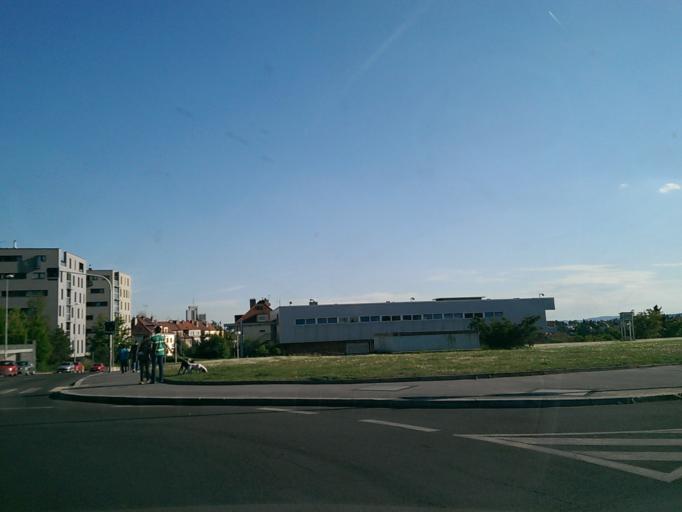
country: CZ
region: Praha
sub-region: Praha 2
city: Vysehrad
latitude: 50.0494
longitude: 14.4285
